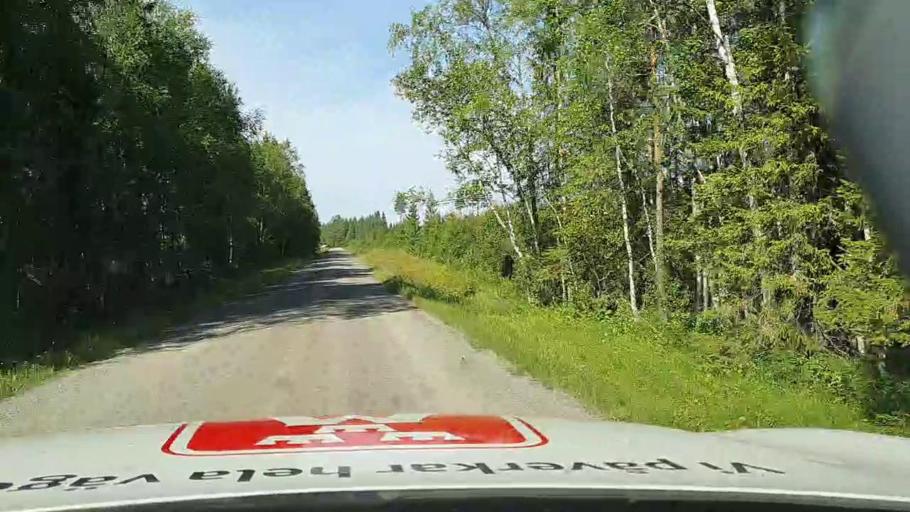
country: SE
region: Jaemtland
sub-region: Stroemsunds Kommun
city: Stroemsund
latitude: 63.7259
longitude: 15.2595
